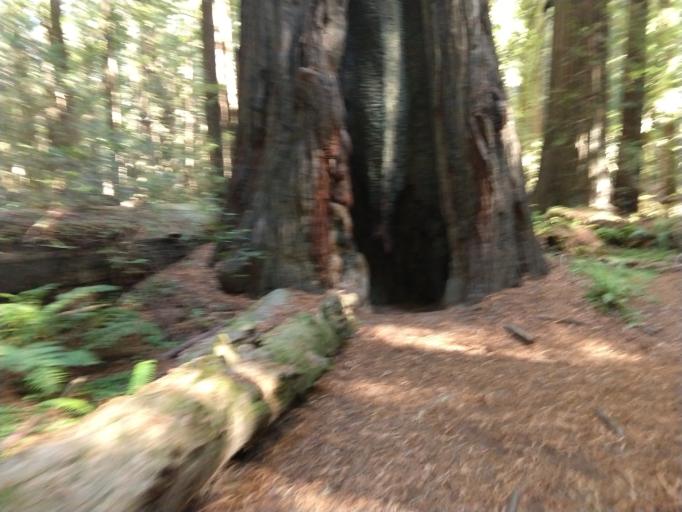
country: US
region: California
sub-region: Humboldt County
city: Rio Dell
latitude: 40.3506
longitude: -123.9260
